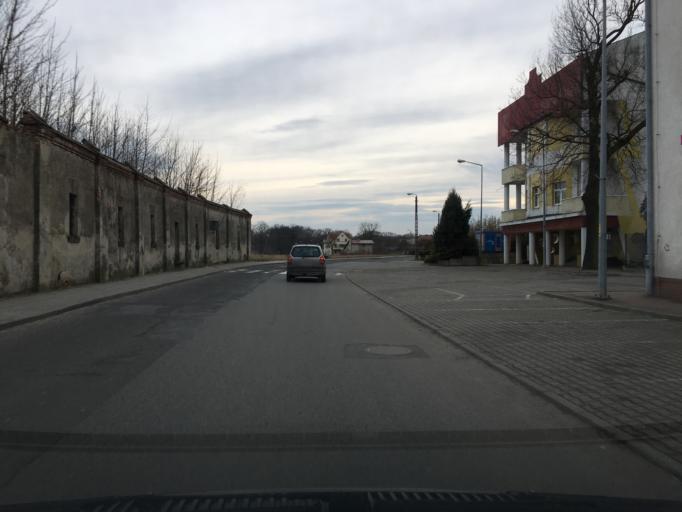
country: PL
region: Opole Voivodeship
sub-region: Powiat kedzierzynsko-kozielski
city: Kozle
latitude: 50.3434
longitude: 18.1449
